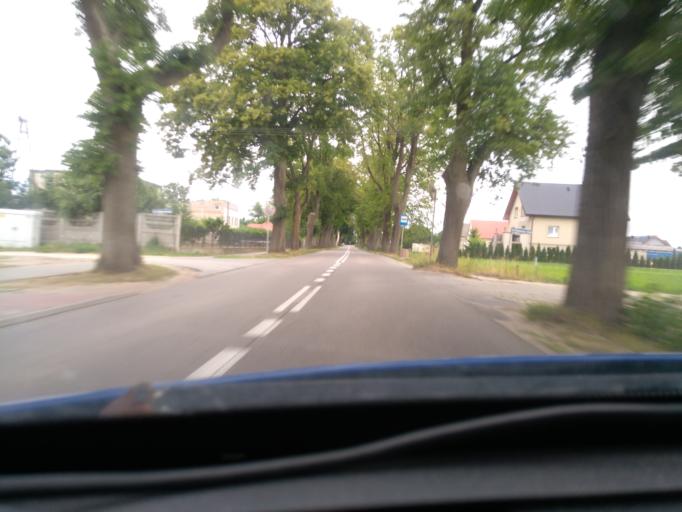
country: PL
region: Pomeranian Voivodeship
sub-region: Powiat kartuski
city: Banino
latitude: 54.3748
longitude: 18.3790
